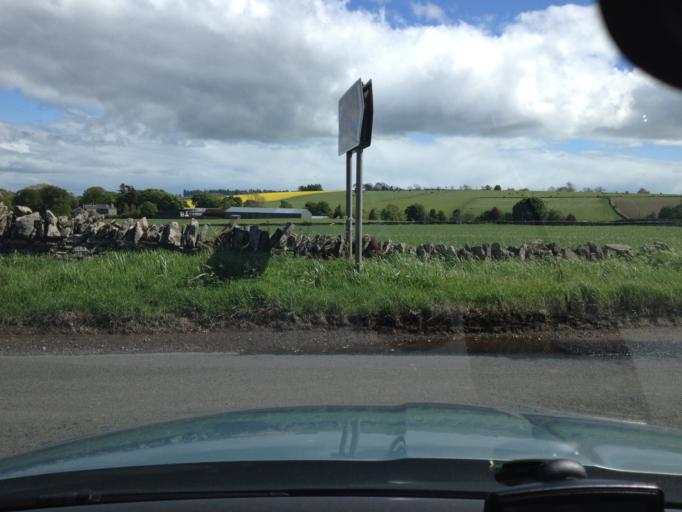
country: GB
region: Scotland
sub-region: Angus
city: Letham
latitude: 56.6920
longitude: -2.7816
